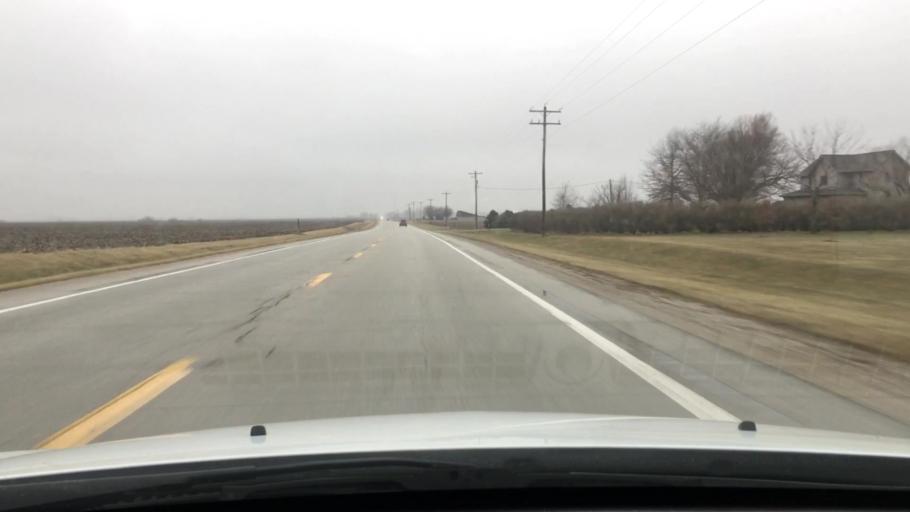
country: US
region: Illinois
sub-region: Livingston County
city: Flanagan
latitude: 40.8718
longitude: -88.8155
